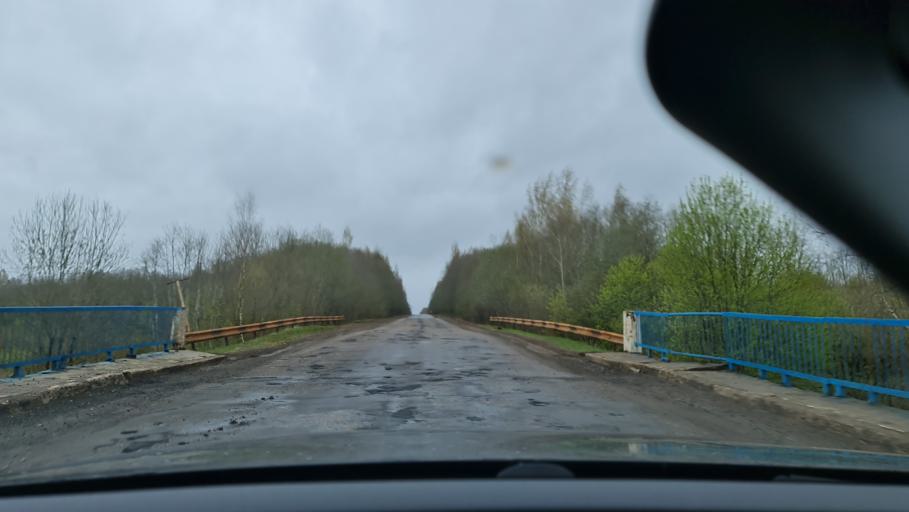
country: RU
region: Novgorod
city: Demyansk
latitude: 57.7418
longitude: 32.5728
